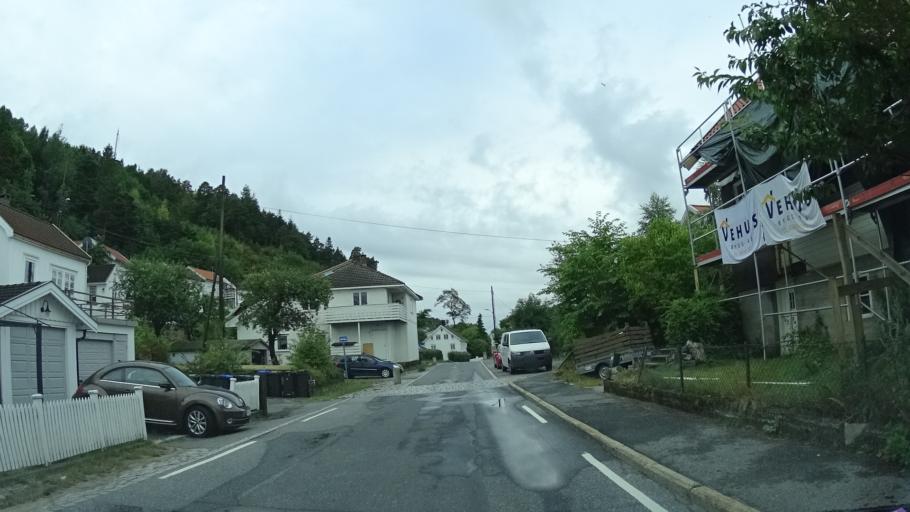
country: NO
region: Aust-Agder
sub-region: Arendal
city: Arendal
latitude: 58.4505
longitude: 8.7557
